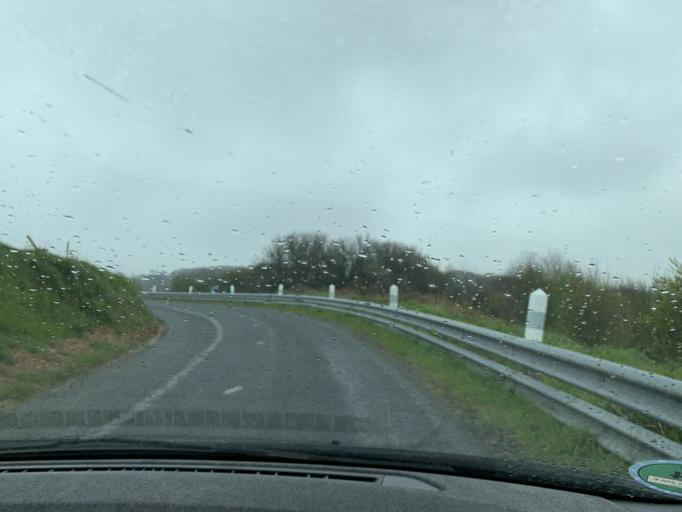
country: FR
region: Haute-Normandie
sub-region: Departement de la Seine-Maritime
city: Etretat
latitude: 49.7127
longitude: 0.2374
